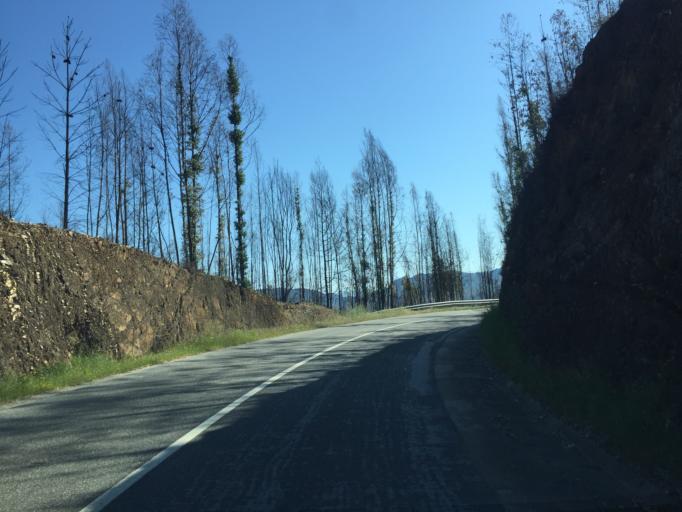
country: PT
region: Coimbra
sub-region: Pampilhosa da Serra
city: Pampilhosa da Serra
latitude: 40.0401
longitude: -7.9142
